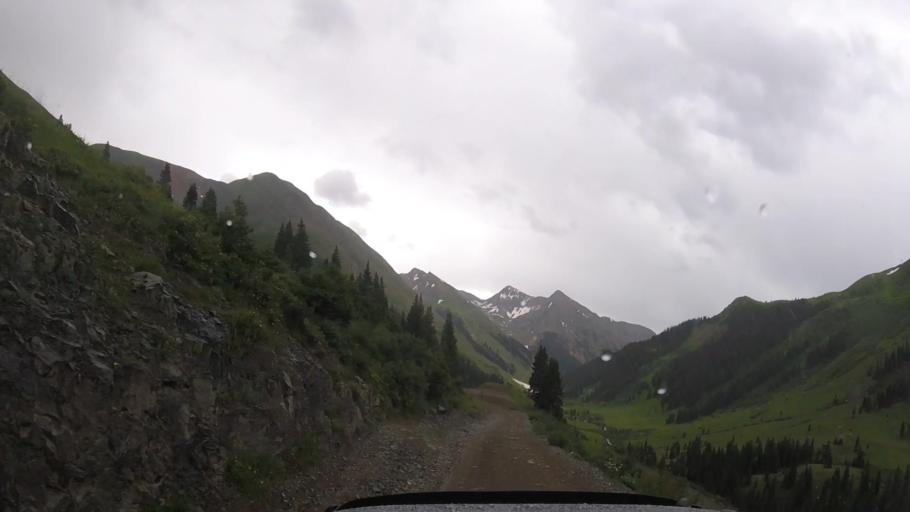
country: US
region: Colorado
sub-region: Ouray County
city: Ouray
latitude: 37.9308
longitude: -107.5665
